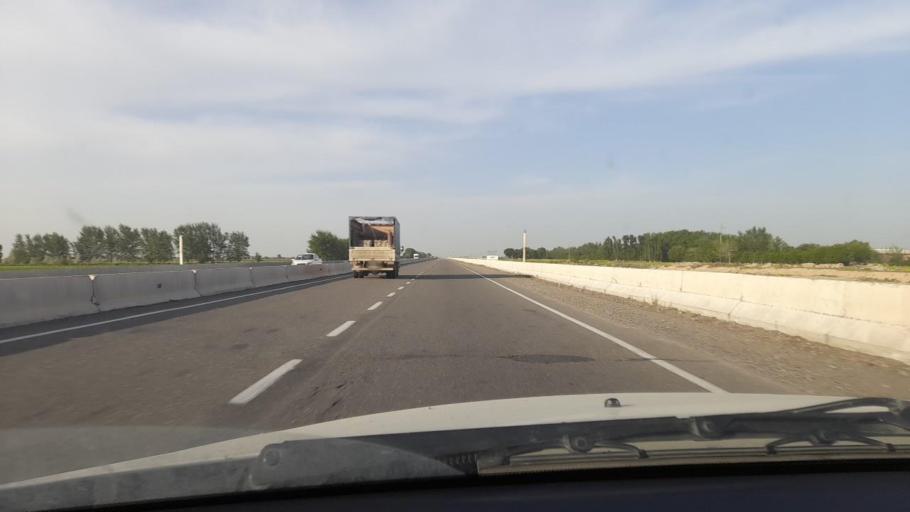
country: UZ
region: Jizzax
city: Paxtakor
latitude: 40.3239
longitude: 68.0995
